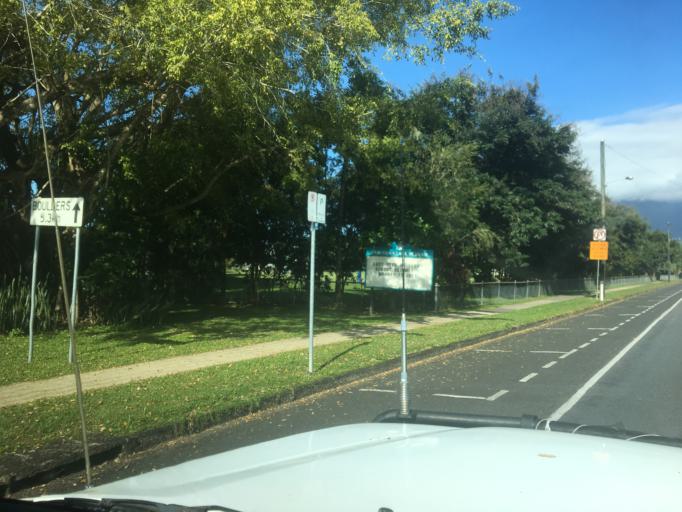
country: AU
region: Queensland
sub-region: Cassowary Coast
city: Innisfail
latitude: -17.3452
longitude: 145.9137
